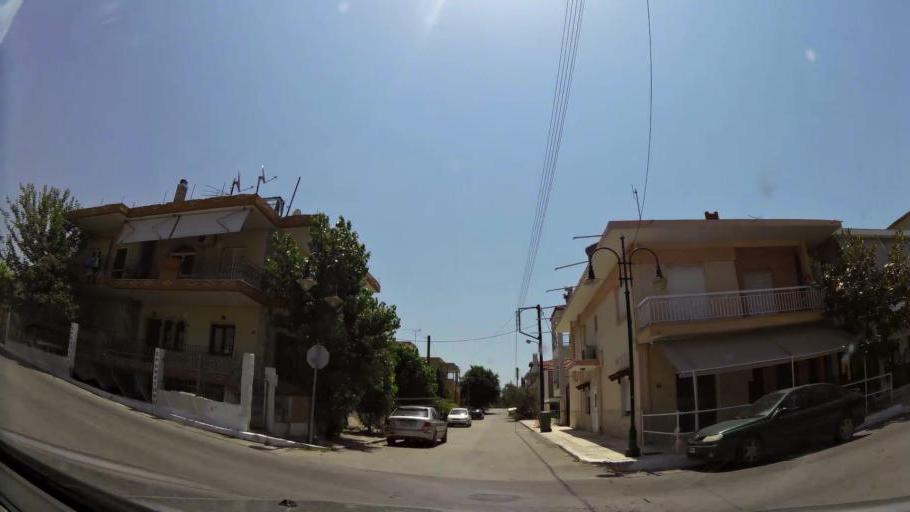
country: GR
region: Central Macedonia
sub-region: Nomos Thessalonikis
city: Nea Michaniona
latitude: 40.4762
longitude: 22.8701
